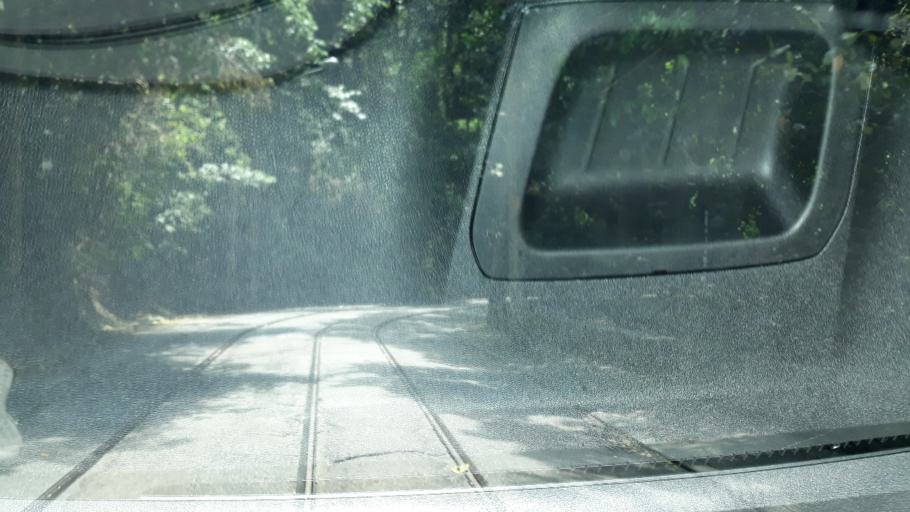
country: BR
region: Rio de Janeiro
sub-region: Rio De Janeiro
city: Rio de Janeiro
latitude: -22.9420
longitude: -43.2097
